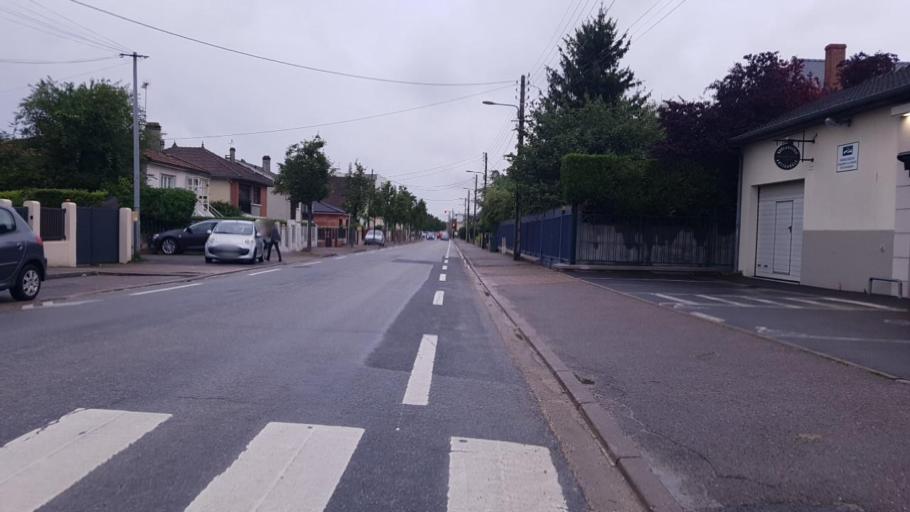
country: FR
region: Champagne-Ardenne
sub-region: Departement de la Marne
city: Saint-Memmie
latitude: 48.9373
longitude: 4.3845
